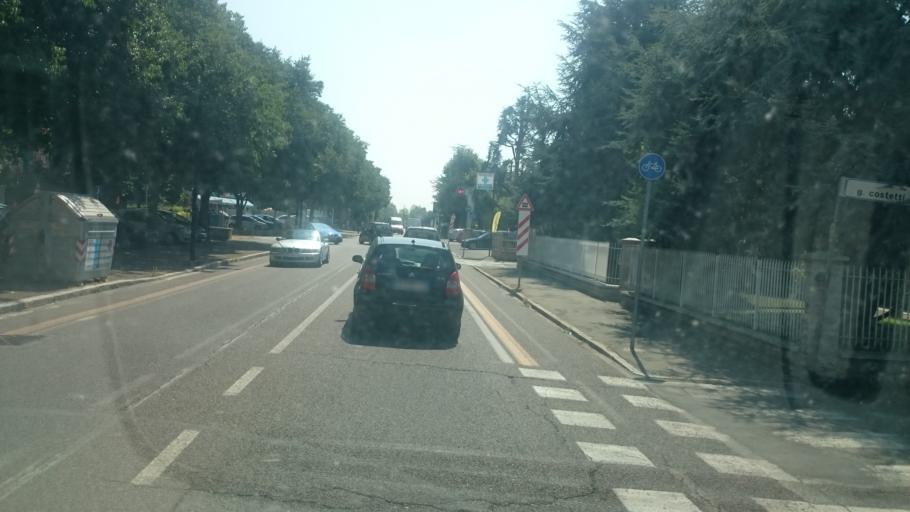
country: IT
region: Emilia-Romagna
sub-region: Provincia di Reggio Emilia
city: Reggio nell'Emilia
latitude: 44.6852
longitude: 10.6511
